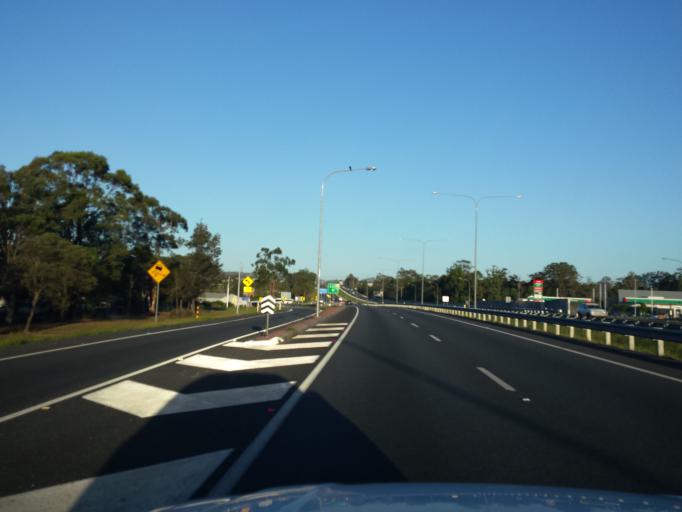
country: AU
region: Queensland
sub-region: Logan
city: Waterford West
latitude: -27.6683
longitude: 153.1232
